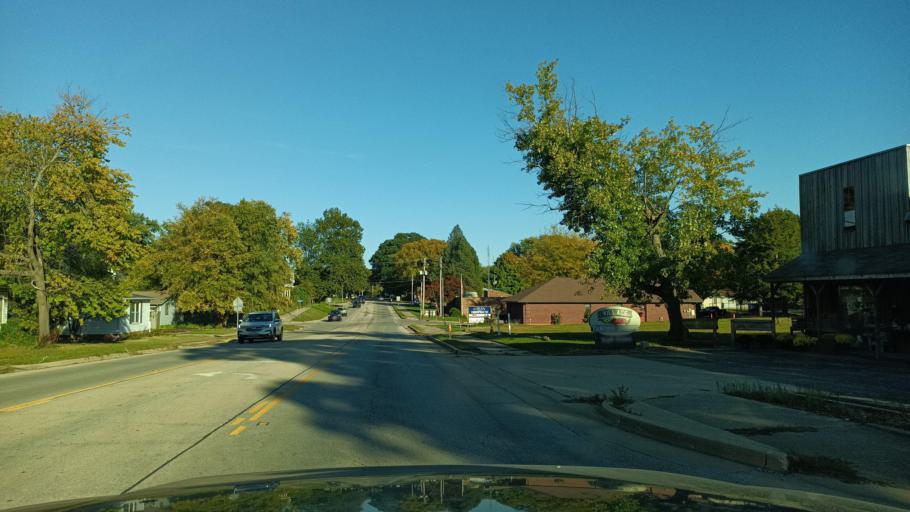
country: US
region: Illinois
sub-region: Champaign County
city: Mahomet
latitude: 40.1919
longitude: -88.4066
